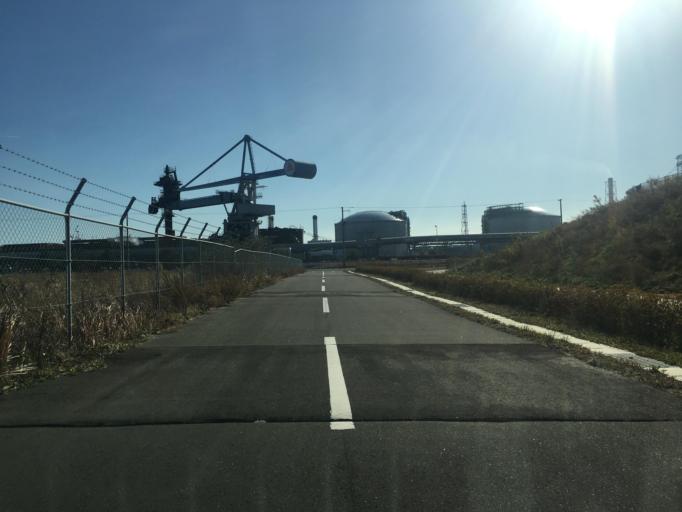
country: JP
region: Miyagi
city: Marumori
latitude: 37.8570
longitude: 140.9503
